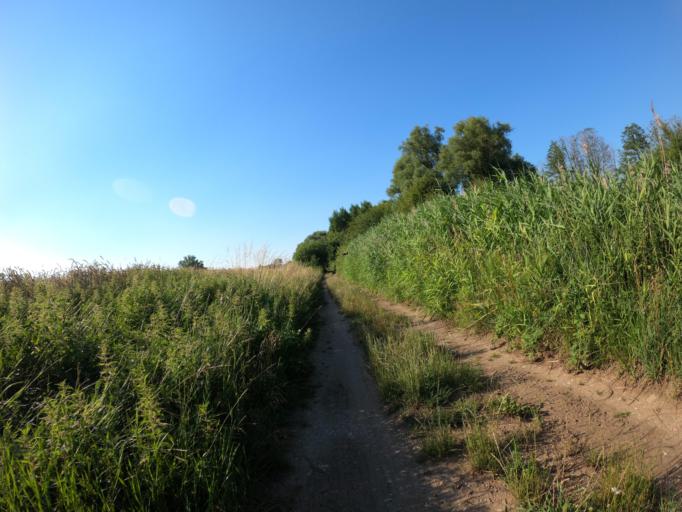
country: DE
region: Brandenburg
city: Gartz
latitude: 53.2330
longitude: 14.3669
